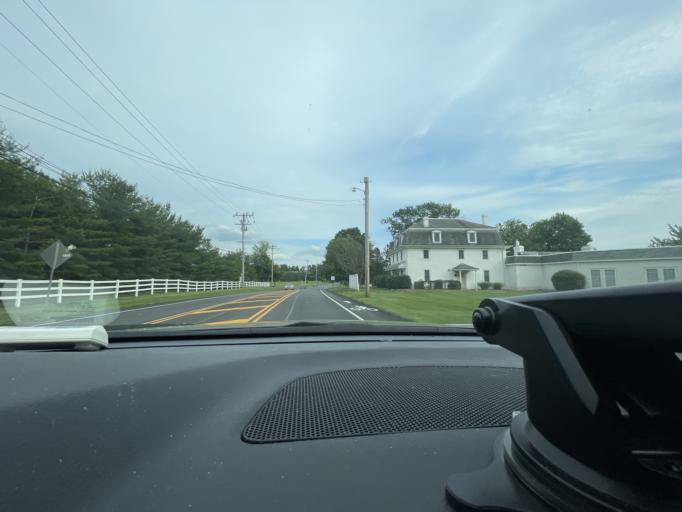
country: US
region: Pennsylvania
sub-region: Montgomery County
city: Blue Bell
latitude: 40.1750
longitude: -75.2713
